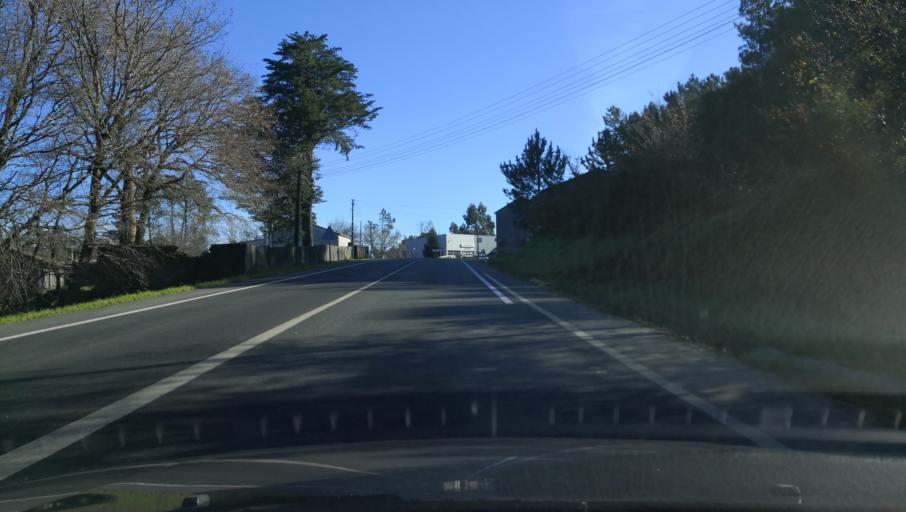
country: ES
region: Galicia
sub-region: Provincia da Coruna
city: Ribeira
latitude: 42.7482
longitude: -8.3440
